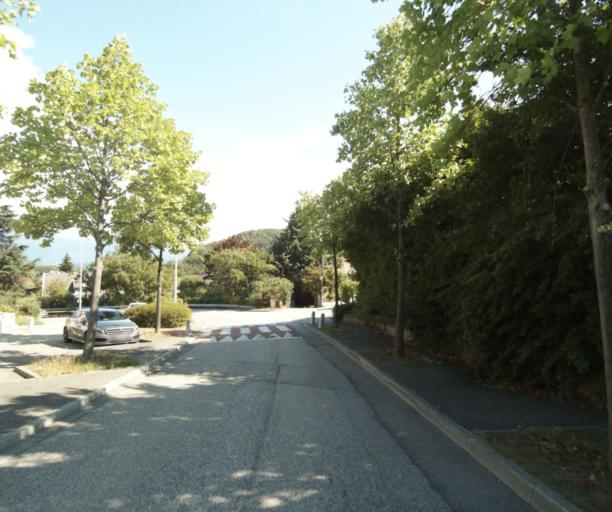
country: FR
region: Rhone-Alpes
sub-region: Departement de l'Isere
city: Seyssins
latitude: 45.1557
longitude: 5.6797
